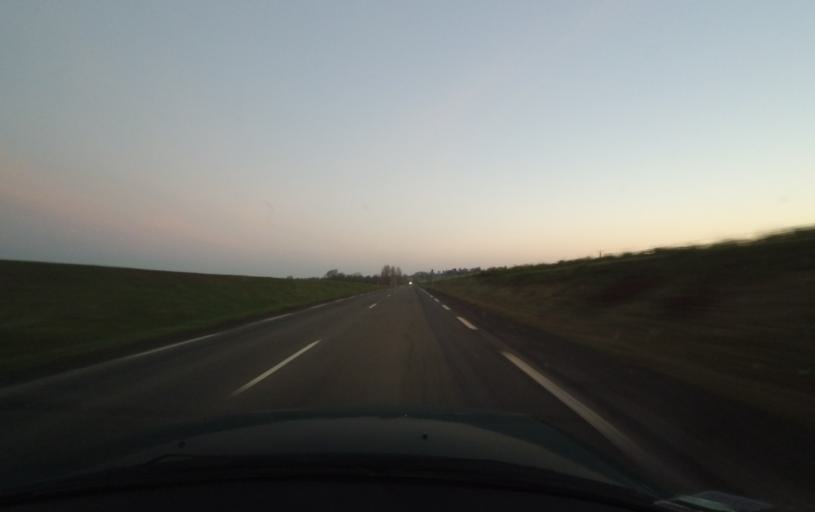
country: FR
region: Pays de la Loire
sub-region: Departement de la Mayenne
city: Soulge-sur-Ouette
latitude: 48.0461
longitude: -0.5734
